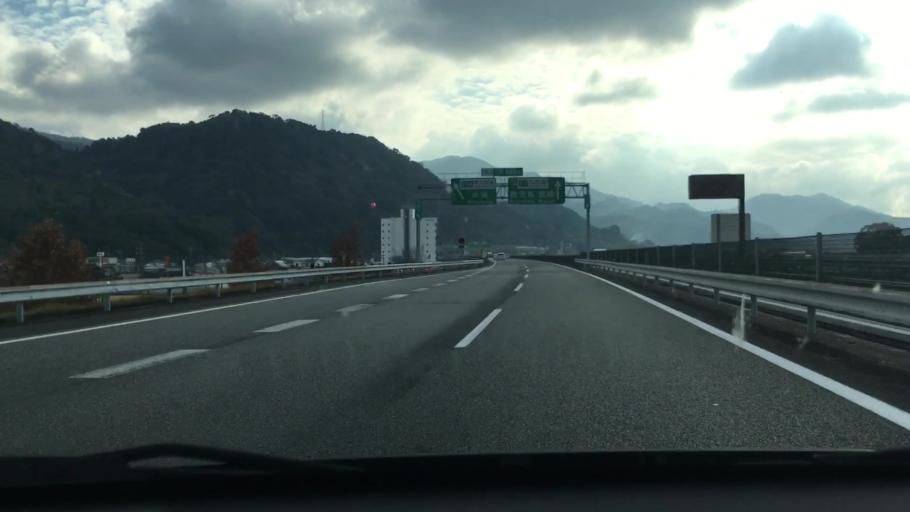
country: JP
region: Kumamoto
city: Yatsushiro
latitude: 32.5107
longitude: 130.6471
